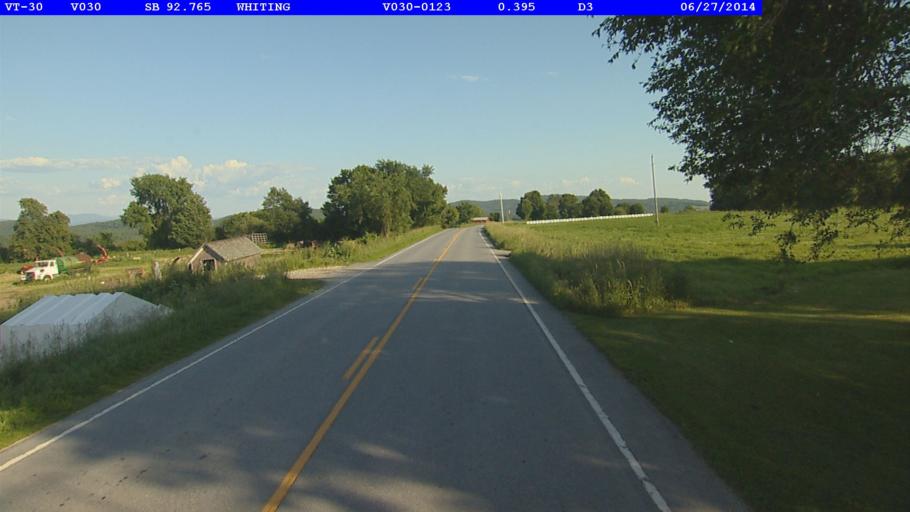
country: US
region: Vermont
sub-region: Rutland County
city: Brandon
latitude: 43.8438
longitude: -73.1961
